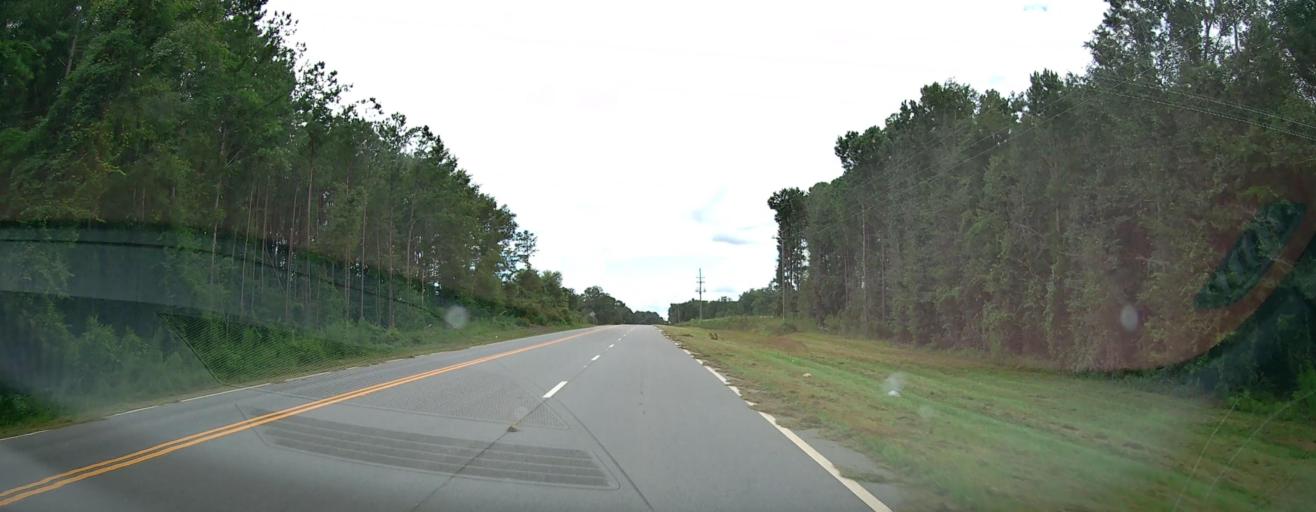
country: US
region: Georgia
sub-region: Schley County
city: Ellaville
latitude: 32.2613
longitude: -84.2101
